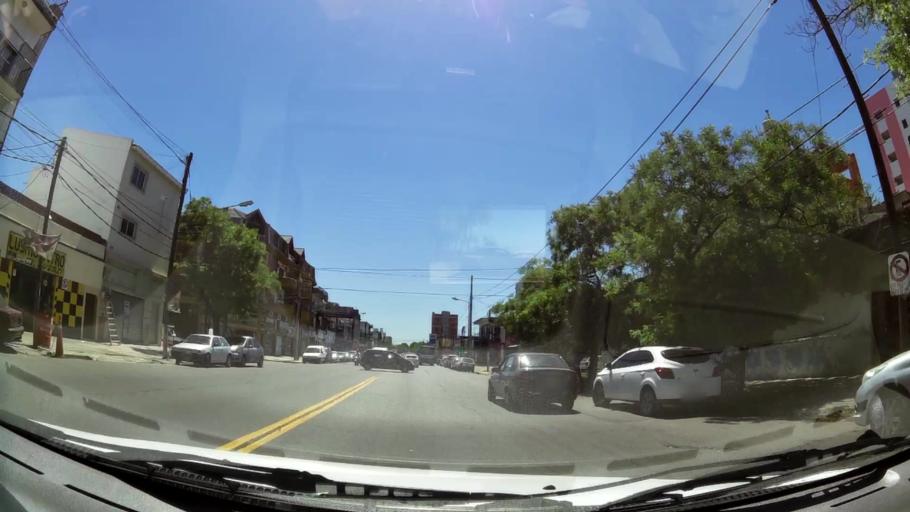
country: AR
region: Buenos Aires
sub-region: Partido de General San Martin
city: General San Martin
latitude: -34.5735
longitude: -58.5449
